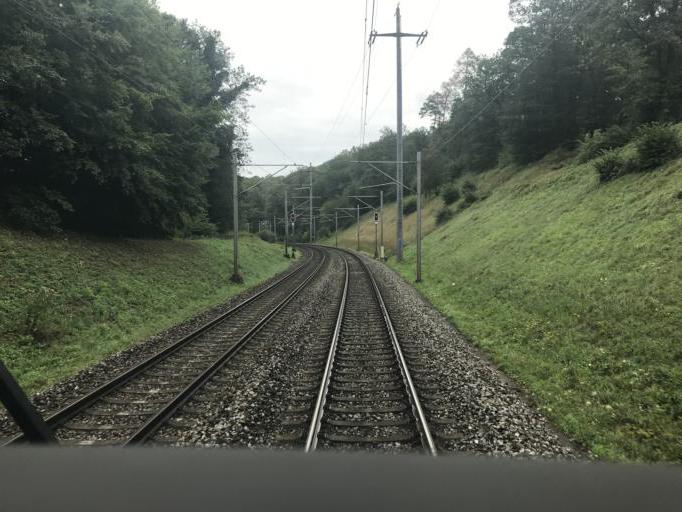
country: CH
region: Zurich
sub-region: Bezirk Buelach
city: Hochfelden
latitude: 47.5388
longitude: 8.5246
